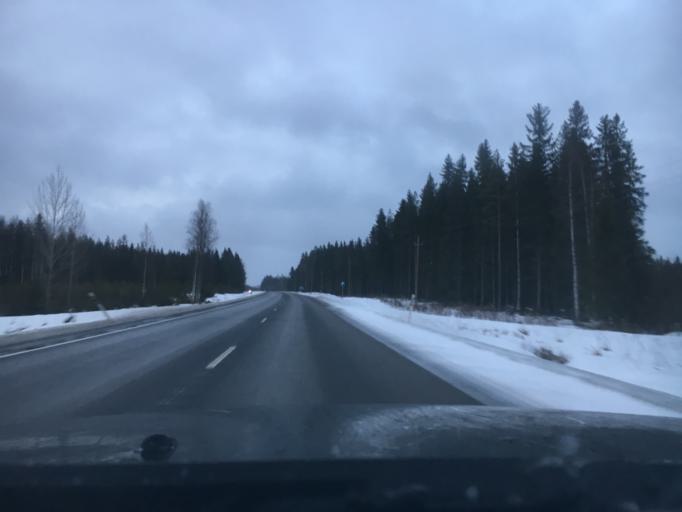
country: FI
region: Central Finland
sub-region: Jyvaeskylae
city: Hankasalmi
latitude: 62.3805
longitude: 26.5963
